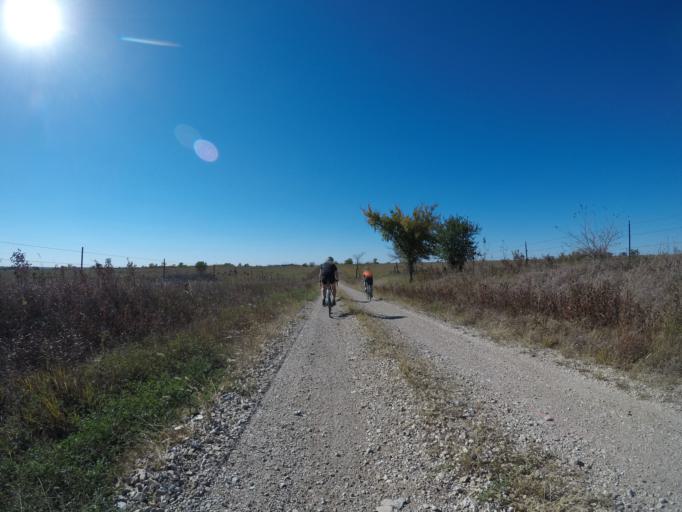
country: US
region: Kansas
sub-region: Wabaunsee County
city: Alma
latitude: 38.9711
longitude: -96.4603
